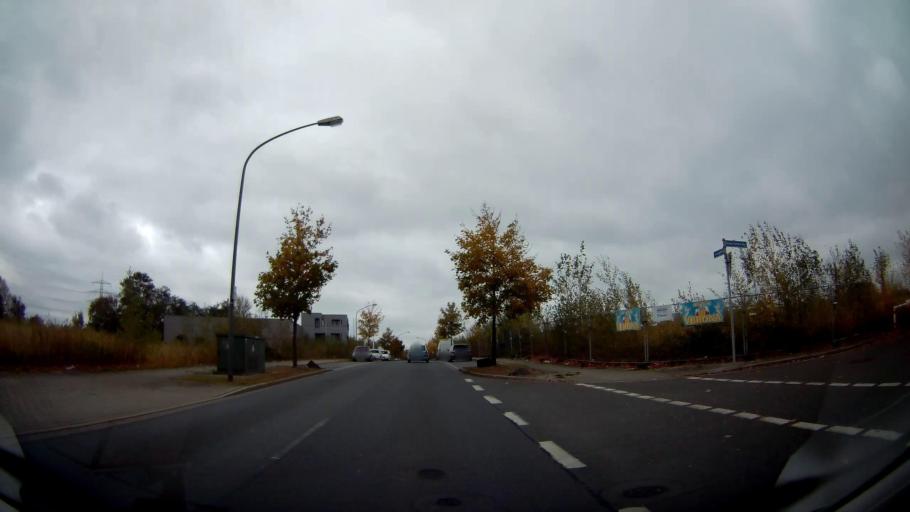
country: DE
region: North Rhine-Westphalia
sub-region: Regierungsbezirk Munster
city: Gladbeck
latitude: 51.5198
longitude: 6.9947
